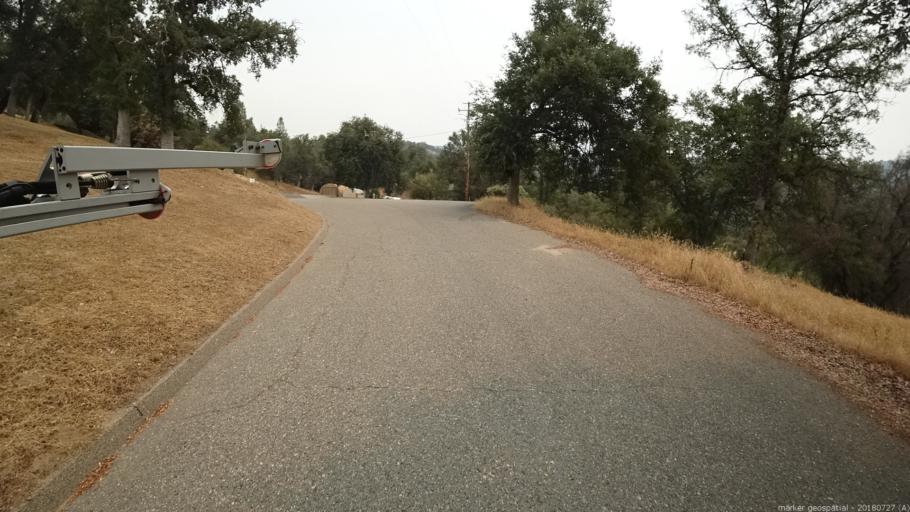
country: US
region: California
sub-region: Madera County
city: Oakhurst
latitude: 37.3322
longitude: -119.6275
